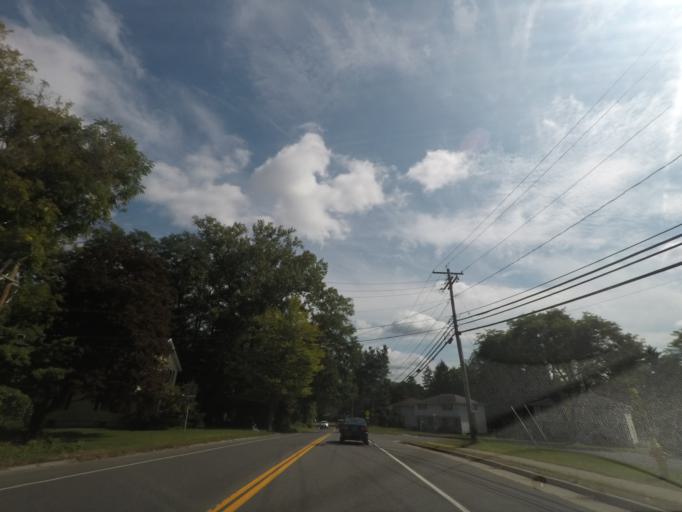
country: US
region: New York
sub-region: Albany County
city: Delmar
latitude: 42.6253
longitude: -73.8526
